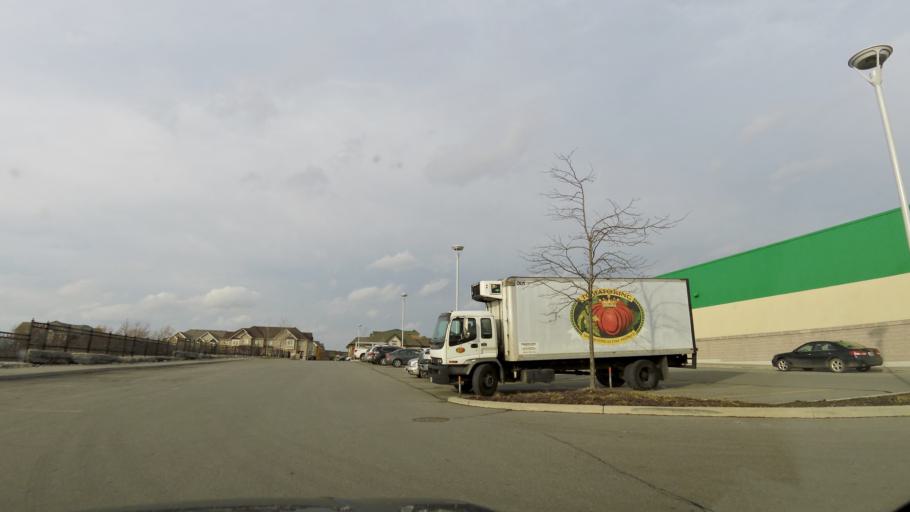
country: CA
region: Ontario
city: Brampton
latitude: 43.7737
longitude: -79.6539
